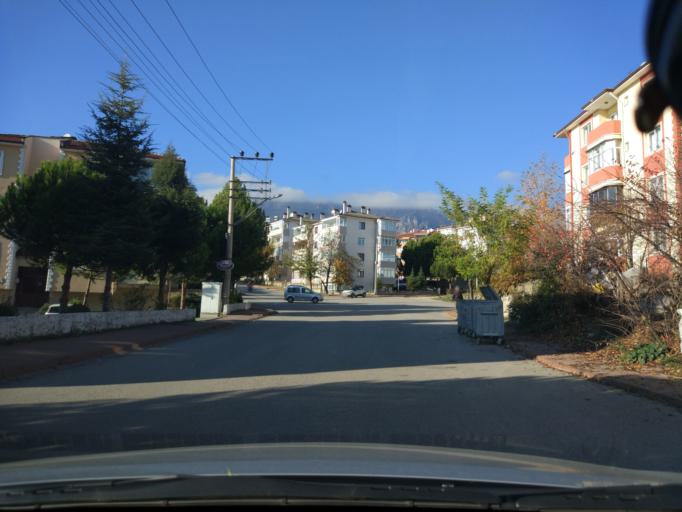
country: TR
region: Karabuk
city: Safranbolu
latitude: 41.2525
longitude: 32.6714
